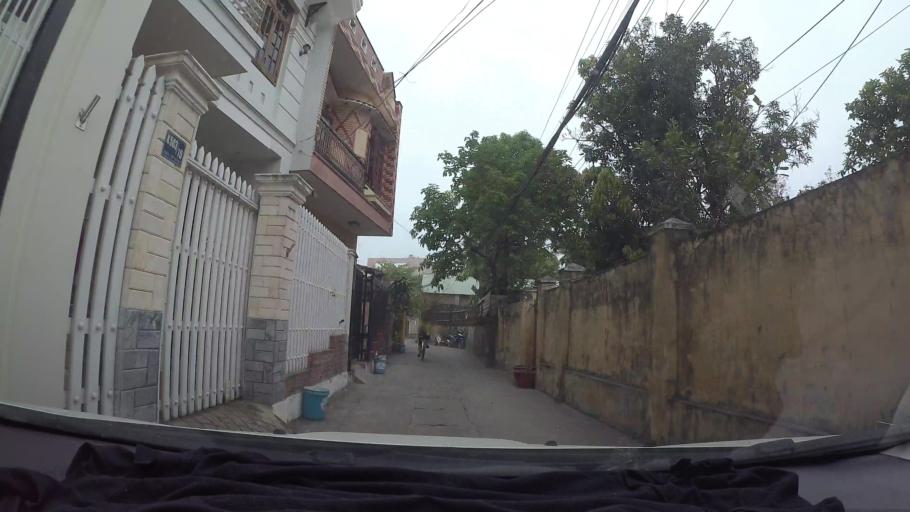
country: VN
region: Da Nang
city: Cam Le
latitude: 16.0415
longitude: 108.2064
